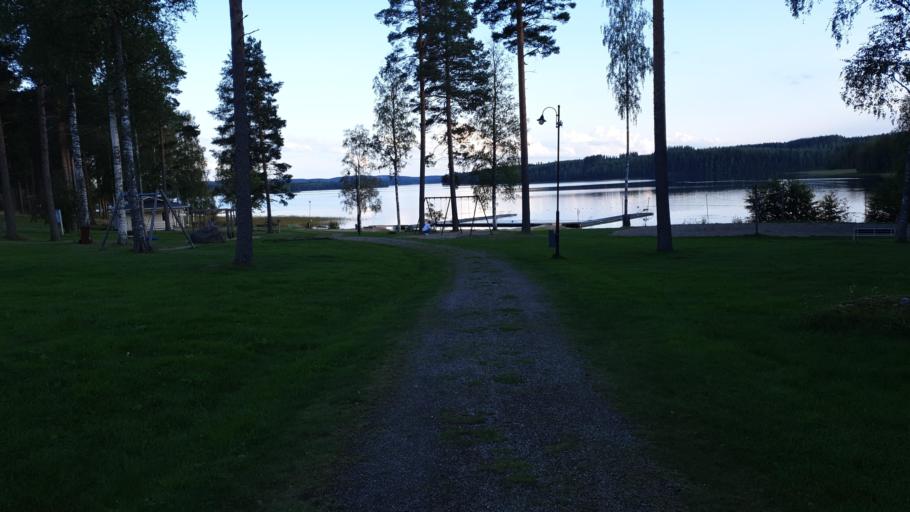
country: FI
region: Northern Savo
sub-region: Koillis-Savo
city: Kaavi
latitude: 62.9747
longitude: 28.4681
